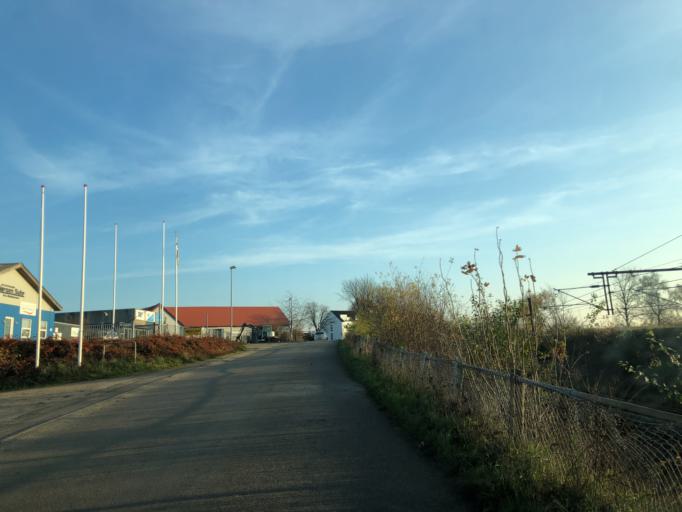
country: DK
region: South Denmark
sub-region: Fredericia Kommune
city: Fredericia
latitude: 55.5795
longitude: 9.7382
